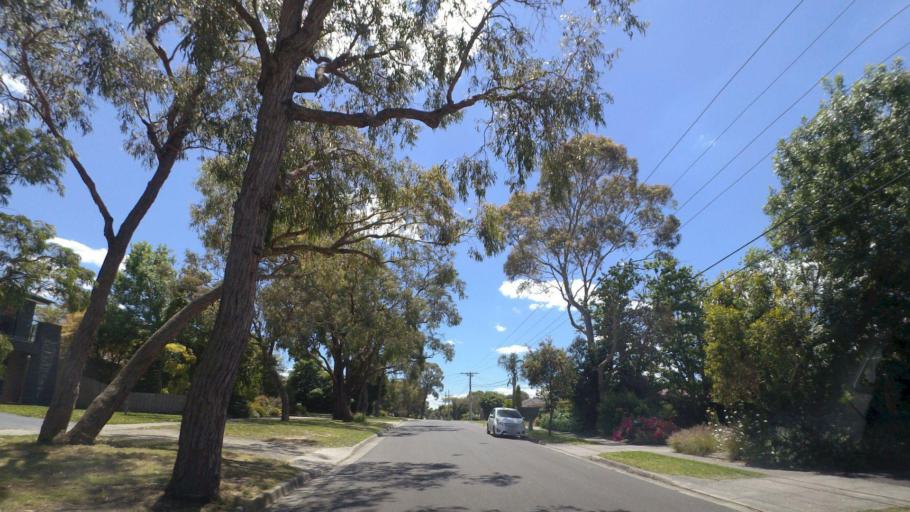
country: AU
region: Victoria
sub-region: Knox
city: Knoxfield
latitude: -37.8851
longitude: 145.2640
